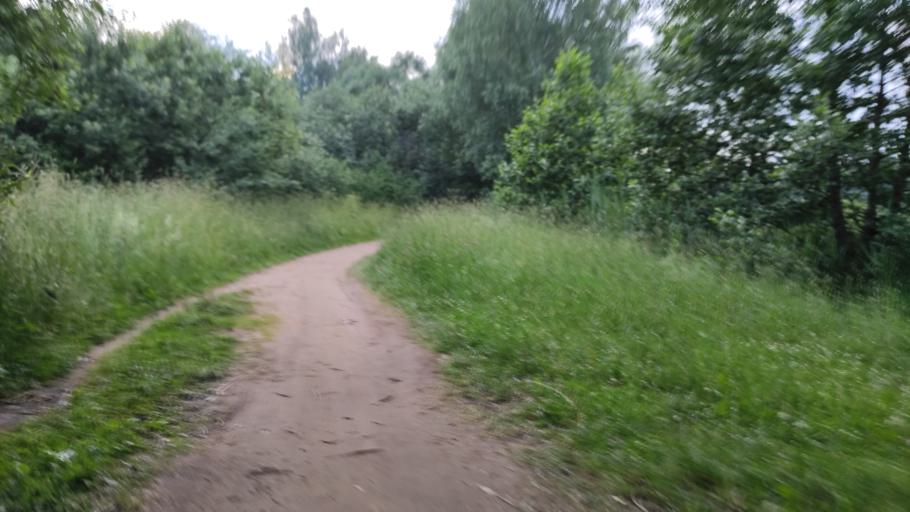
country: BY
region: Minsk
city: Zhdanovichy
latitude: 53.9628
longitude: 27.4427
